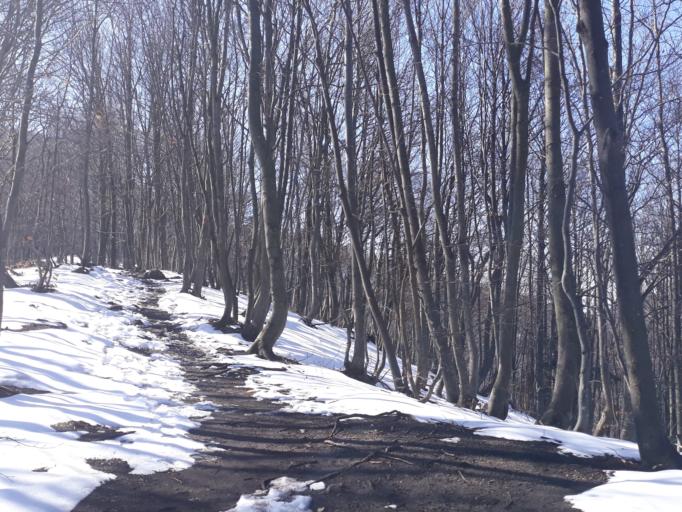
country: HR
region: Varazdinska
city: Ivanec
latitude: 46.1860
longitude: 16.1238
